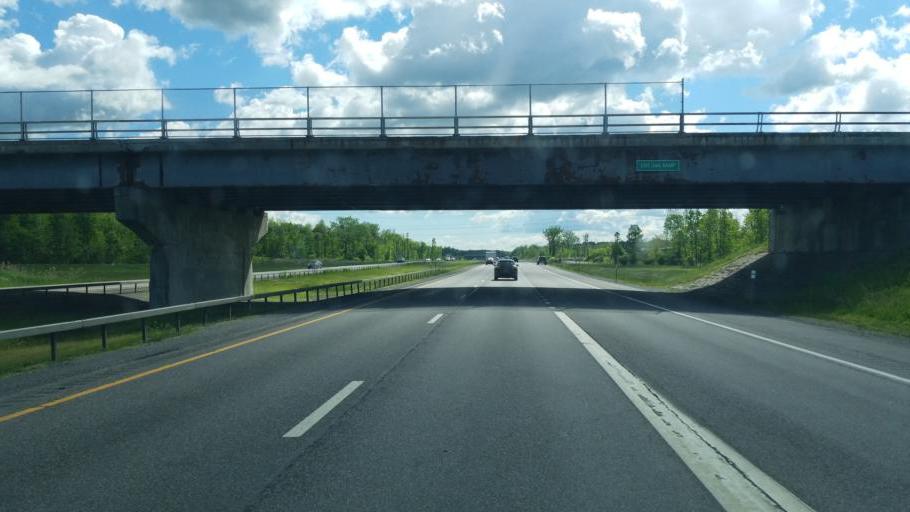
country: US
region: New York
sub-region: Onondaga County
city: East Syracuse
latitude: 43.0946
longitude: -76.0439
